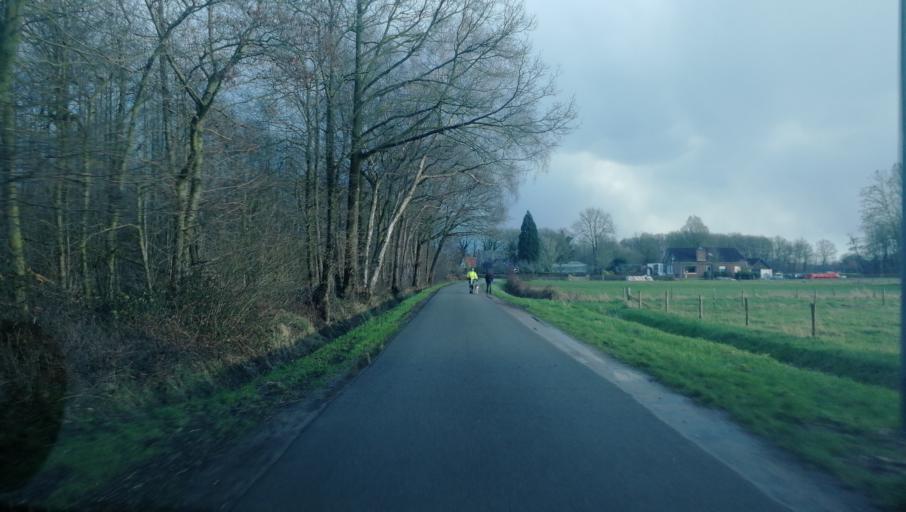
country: NL
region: Limburg
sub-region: Gemeente Peel en Maas
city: Maasbree
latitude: 51.3473
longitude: 6.0319
